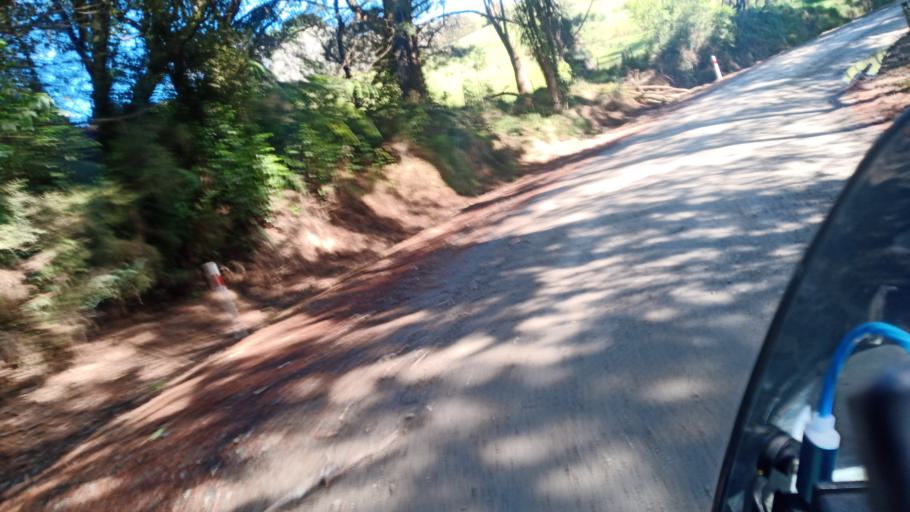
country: NZ
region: Gisborne
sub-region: Gisborne District
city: Gisborne
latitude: -37.9943
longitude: 178.3090
